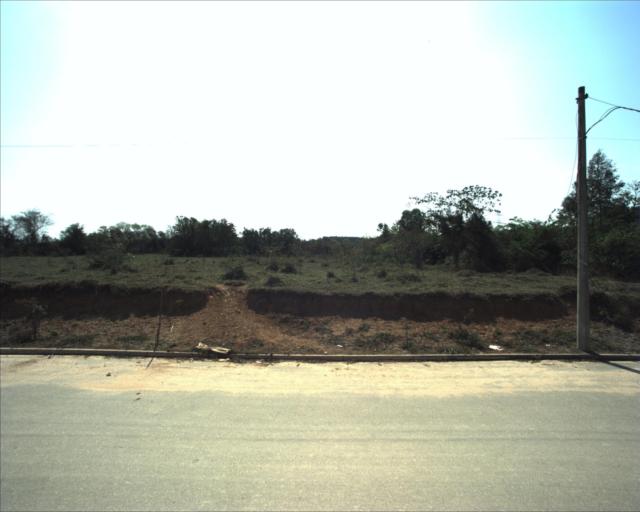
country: BR
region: Sao Paulo
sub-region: Sorocaba
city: Sorocaba
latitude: -23.4191
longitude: -47.4436
